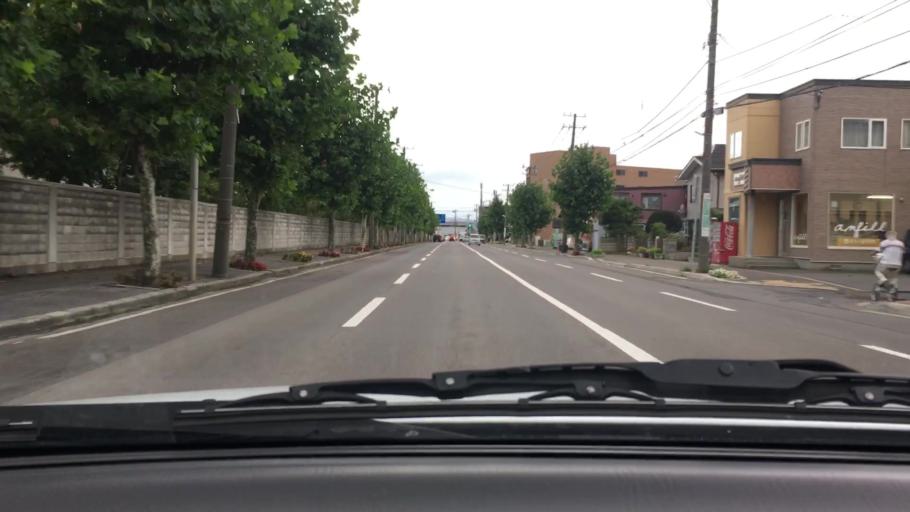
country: JP
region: Hokkaido
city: Hakodate
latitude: 41.8009
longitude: 140.7281
